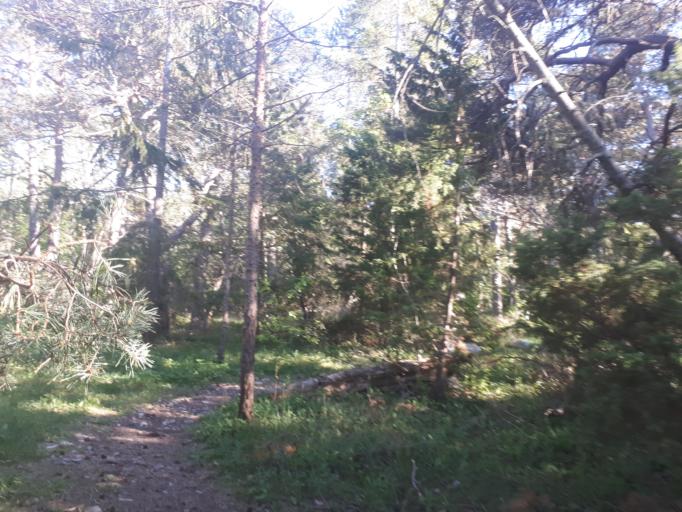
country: SE
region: Gotland
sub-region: Gotland
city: Vibble
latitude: 57.6116
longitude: 18.2498
